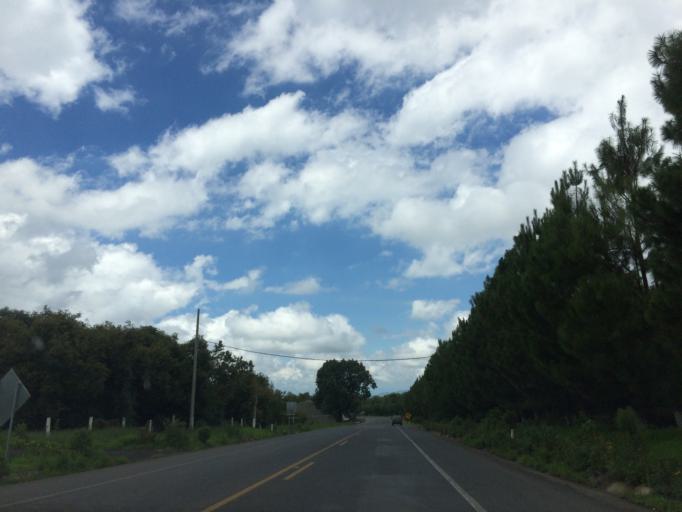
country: MX
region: Michoacan
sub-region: Uruapan
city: Nuevo Zirosto
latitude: 19.5485
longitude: -102.3375
